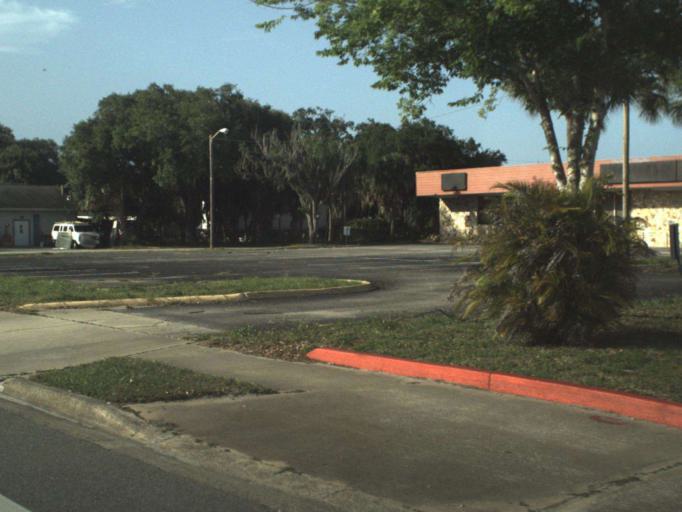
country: US
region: Florida
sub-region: Volusia County
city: New Smyrna Beach
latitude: 29.0160
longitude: -80.9222
